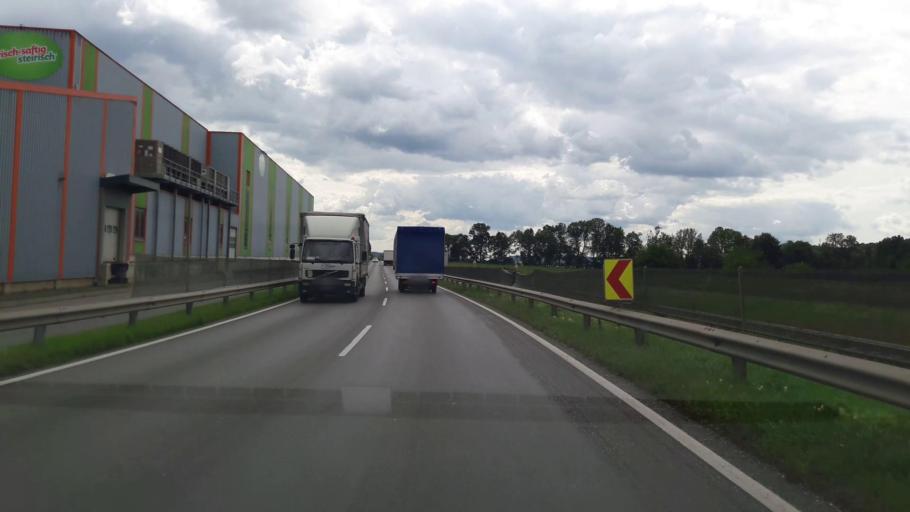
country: AT
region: Styria
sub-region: Politischer Bezirk Weiz
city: Sankt Ruprecht an der Raab
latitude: 47.1363
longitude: 15.6804
